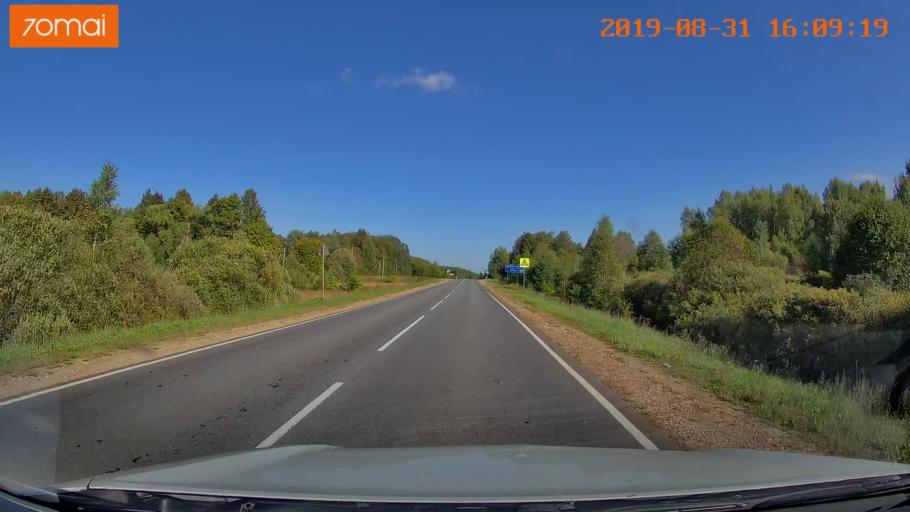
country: RU
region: Kaluga
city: Yukhnov
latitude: 54.5889
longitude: 35.3956
